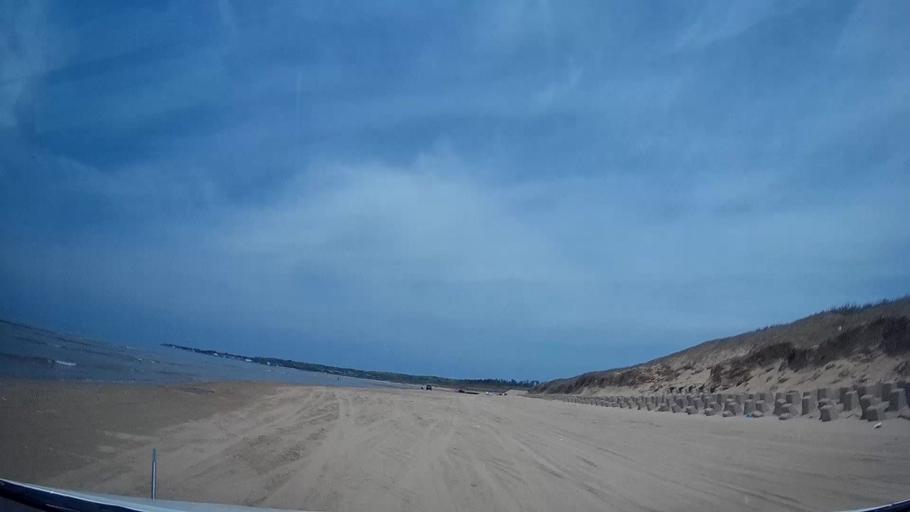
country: JP
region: Ishikawa
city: Hakui
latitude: 36.9001
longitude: 136.7671
